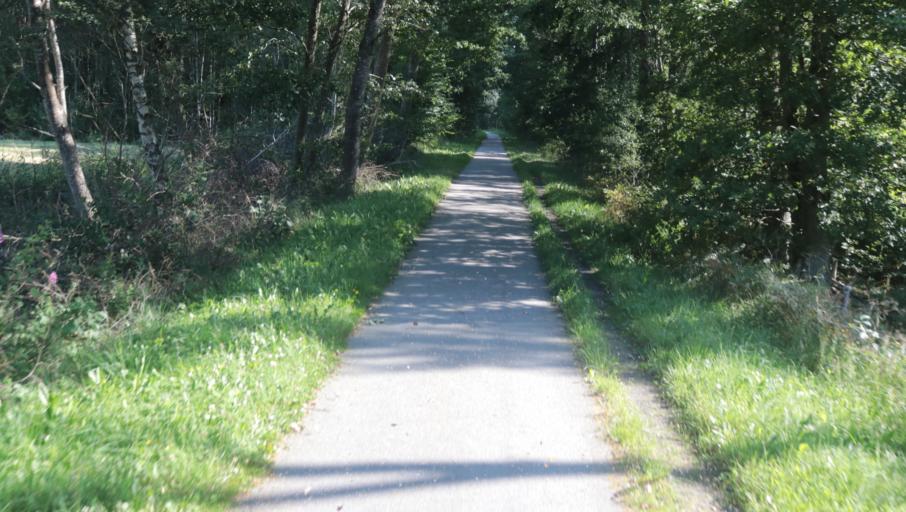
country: SE
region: Blekinge
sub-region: Karlshamns Kommun
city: Svangsta
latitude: 56.2462
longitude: 14.7942
